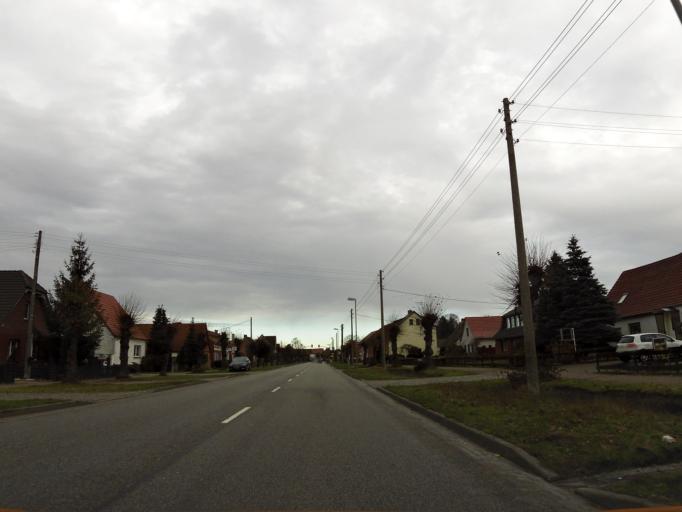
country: DE
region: Saxony-Anhalt
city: Letzlingen
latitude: 52.4423
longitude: 11.4841
